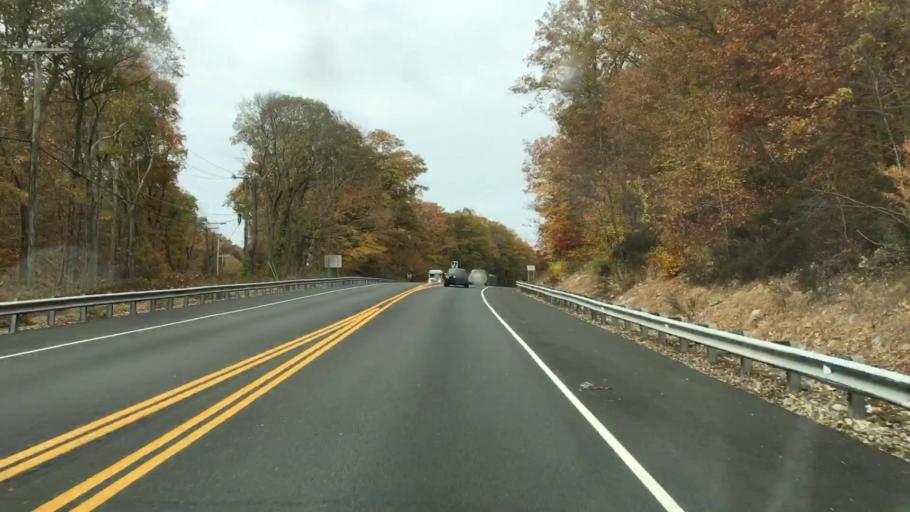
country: US
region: Connecticut
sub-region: Tolland County
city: Rockville
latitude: 41.7870
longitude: -72.4408
